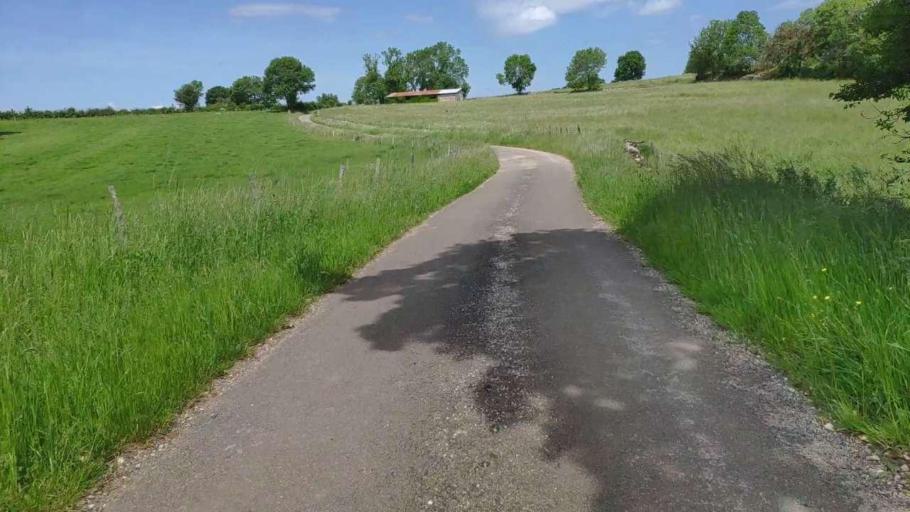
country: FR
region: Franche-Comte
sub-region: Departement du Jura
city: Perrigny
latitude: 46.7491
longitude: 5.6376
